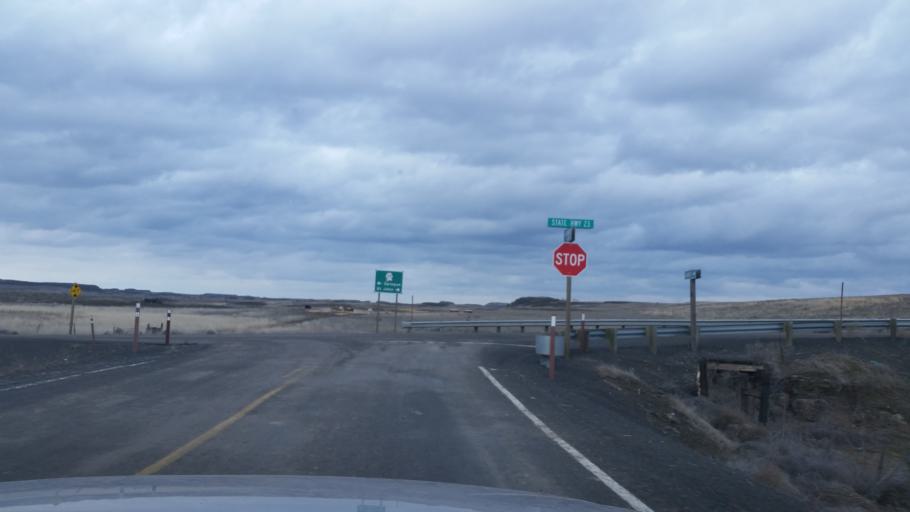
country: US
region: Washington
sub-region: Spokane County
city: Medical Lake
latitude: 47.2122
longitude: -117.8939
